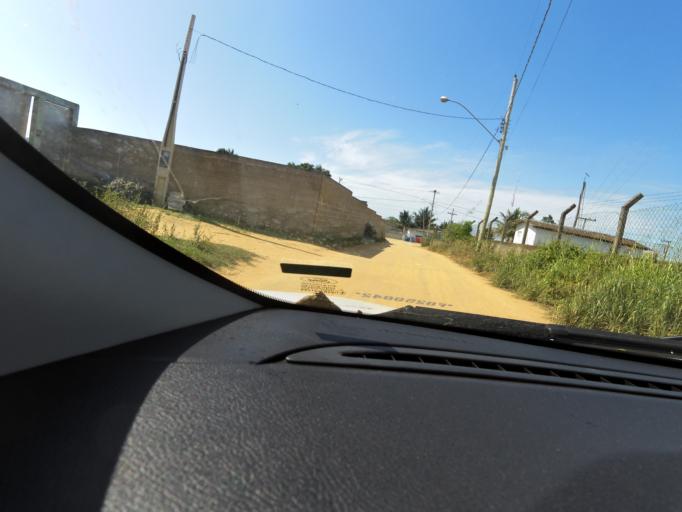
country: BR
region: Espirito Santo
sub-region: Guarapari
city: Guarapari
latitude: -20.6524
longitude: -40.5204
